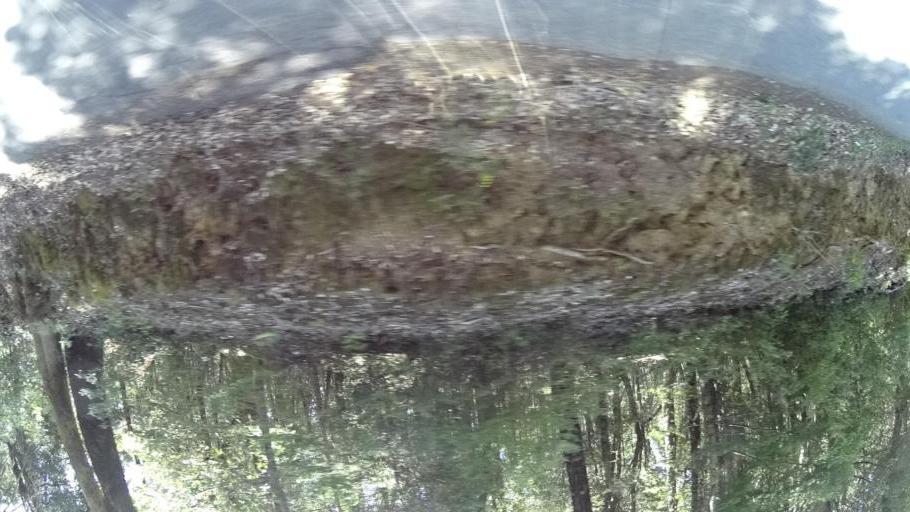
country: US
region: California
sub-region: Humboldt County
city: Redway
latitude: 40.0890
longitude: -123.9479
